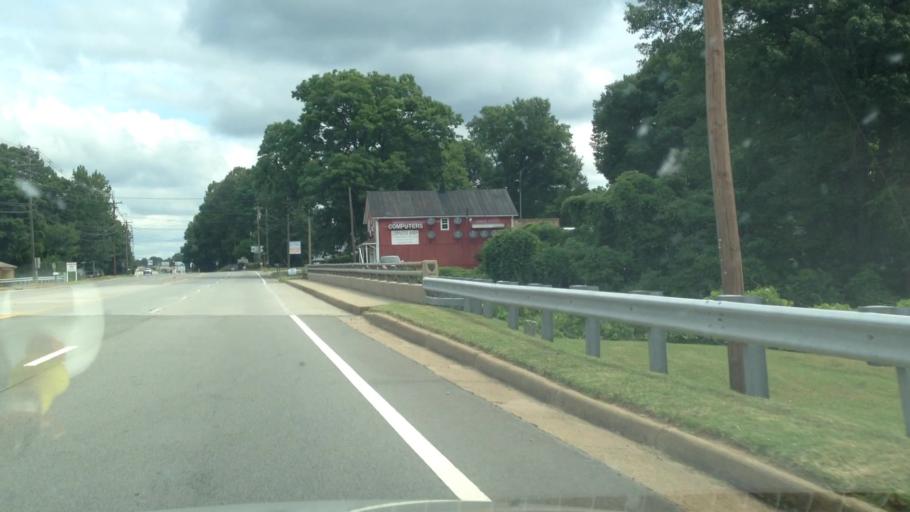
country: US
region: Virginia
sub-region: Pittsylvania County
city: Mount Hermon
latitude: 36.6789
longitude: -79.3734
